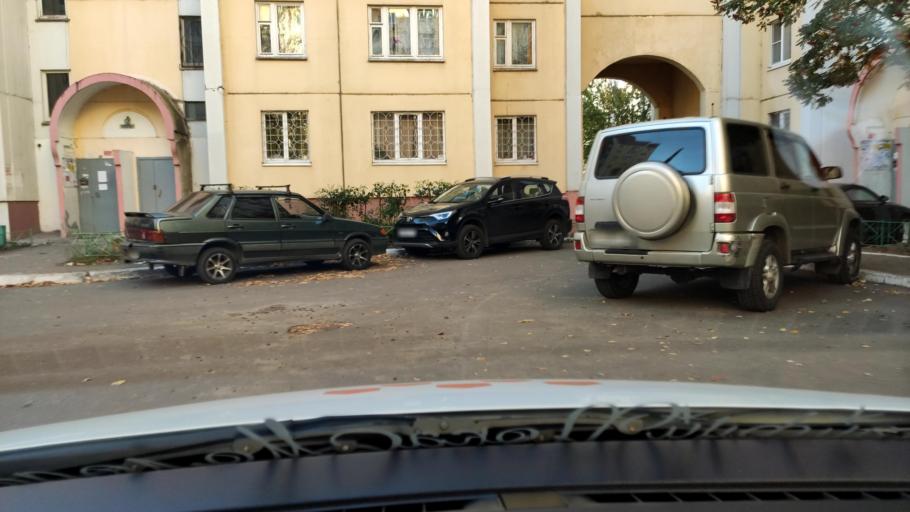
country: RU
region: Voronezj
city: Voronezh
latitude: 51.7105
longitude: 39.1876
